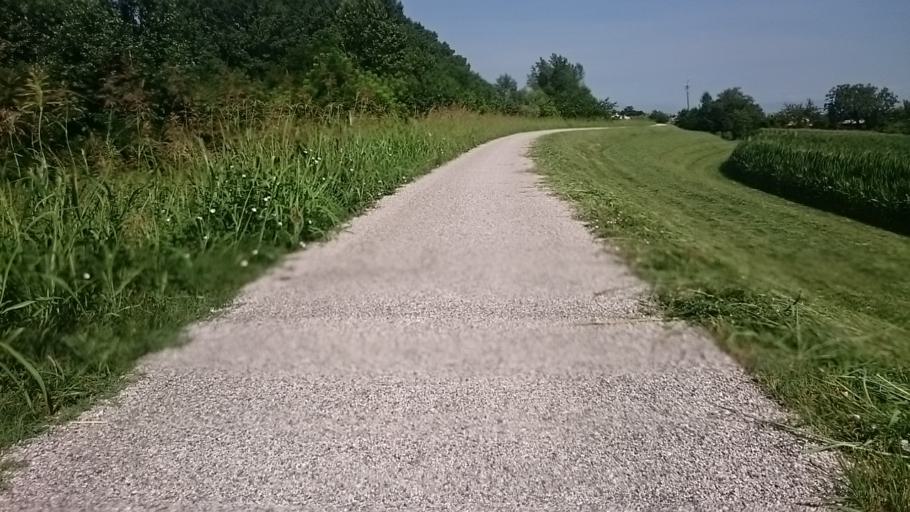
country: IT
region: Veneto
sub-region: Provincia di Padova
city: Saccolongo
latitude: 45.4051
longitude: 11.7565
